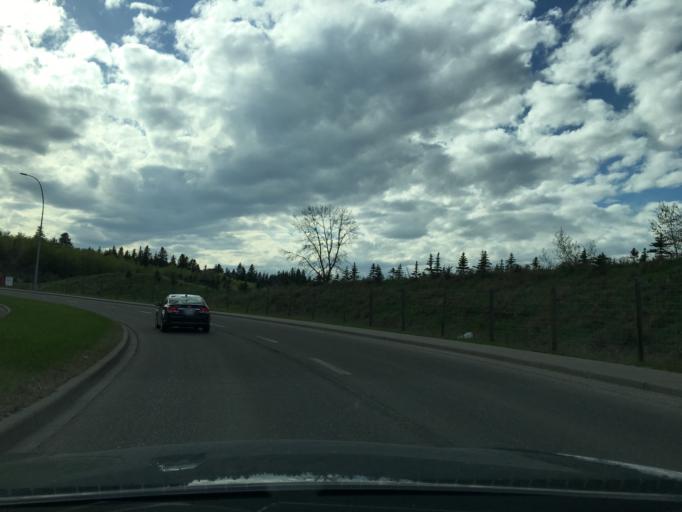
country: CA
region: Alberta
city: Calgary
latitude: 50.9270
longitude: -114.0743
